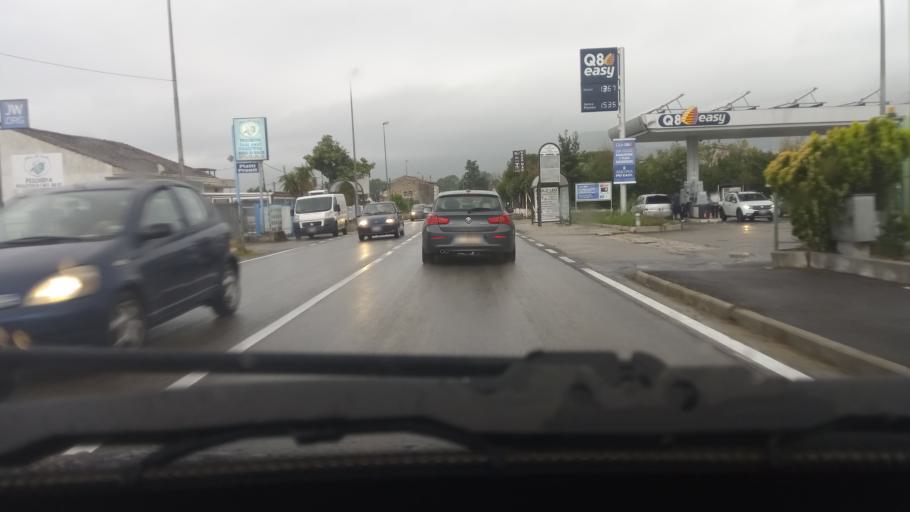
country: IT
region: Latium
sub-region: Provincia di Latina
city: Penitro
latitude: 41.2624
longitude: 13.6832
